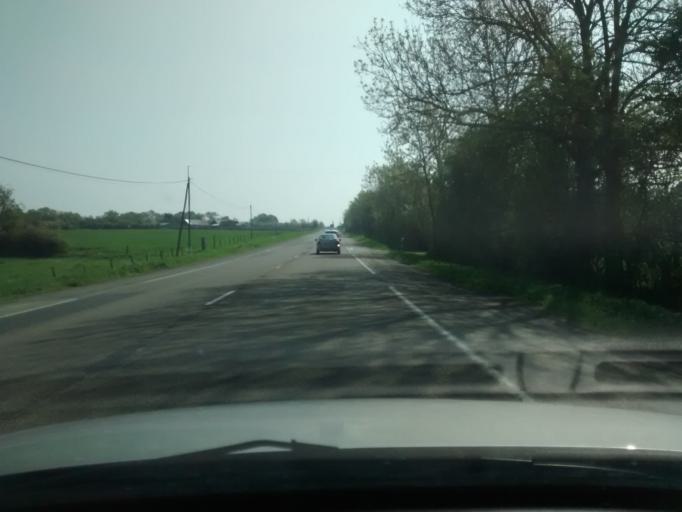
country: FR
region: Pays de la Loire
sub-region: Departement de la Mayenne
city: Soulge-sur-Ouette
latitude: 48.0616
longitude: -0.5893
